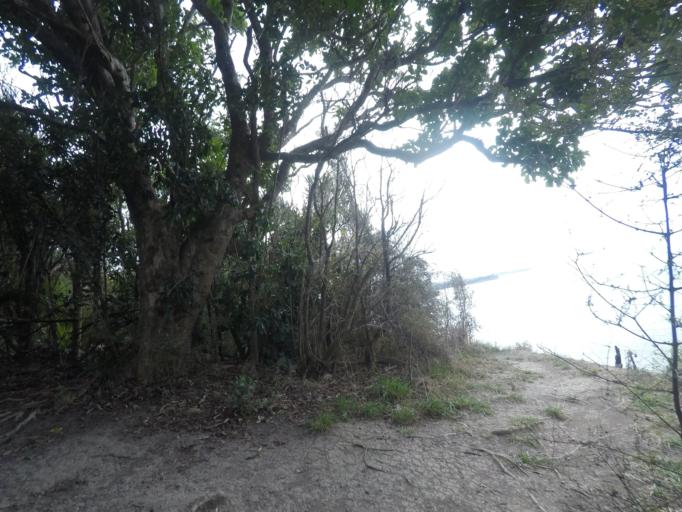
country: NZ
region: Auckland
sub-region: Auckland
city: Rothesay Bay
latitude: -36.6567
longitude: 174.7276
